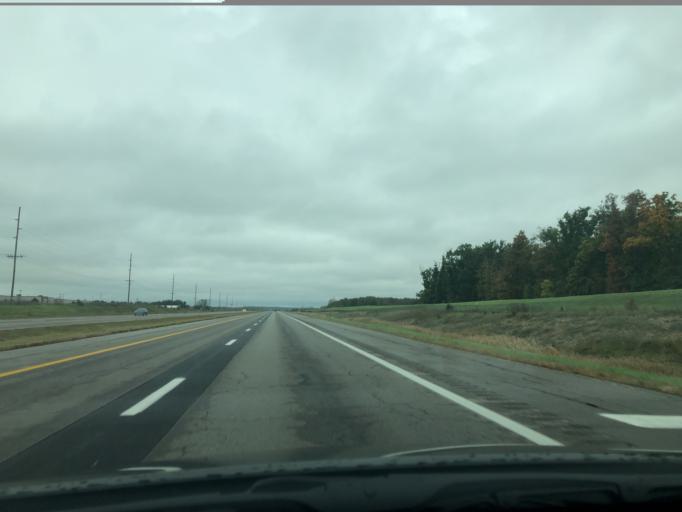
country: US
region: Ohio
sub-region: Champaign County
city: North Lewisburg
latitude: 40.2969
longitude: -83.5570
